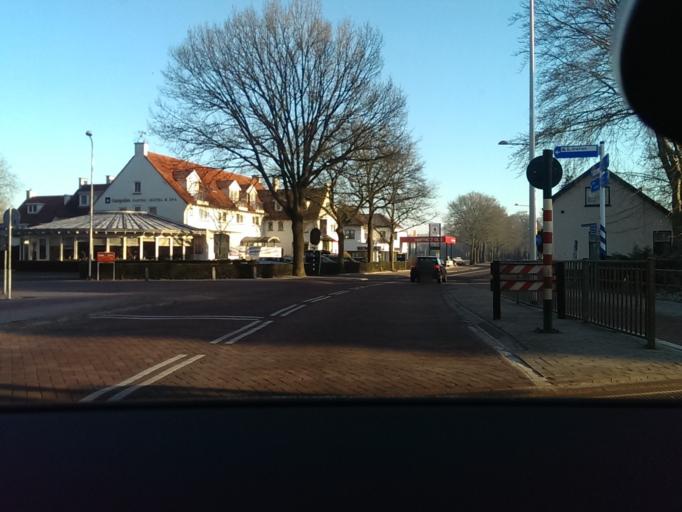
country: NL
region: Overijssel
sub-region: Gemeente Twenterand
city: Den Ham
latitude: 52.5099
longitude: 6.4194
